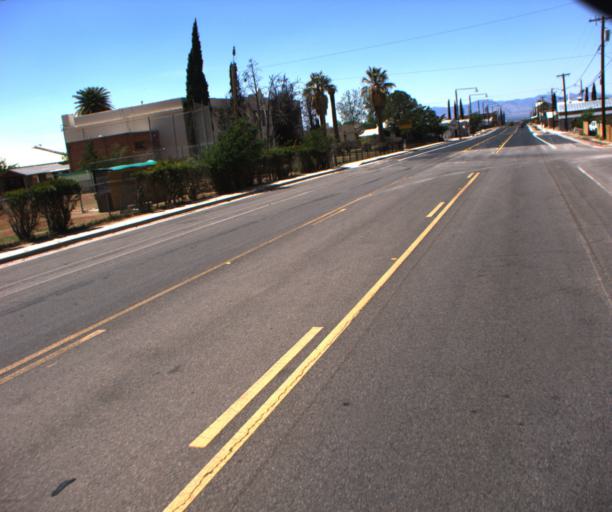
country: US
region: Arizona
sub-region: Cochise County
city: Tombstone
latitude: 31.7124
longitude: -110.0630
